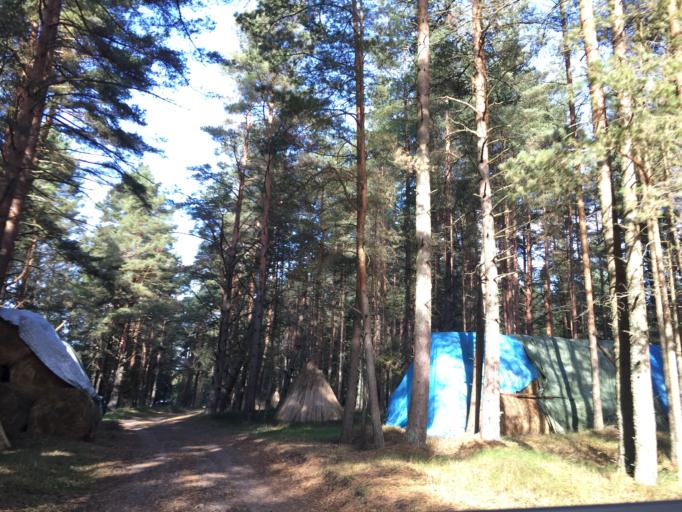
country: LV
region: Mesraga
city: Mersrags
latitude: 57.2582
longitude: 23.1362
